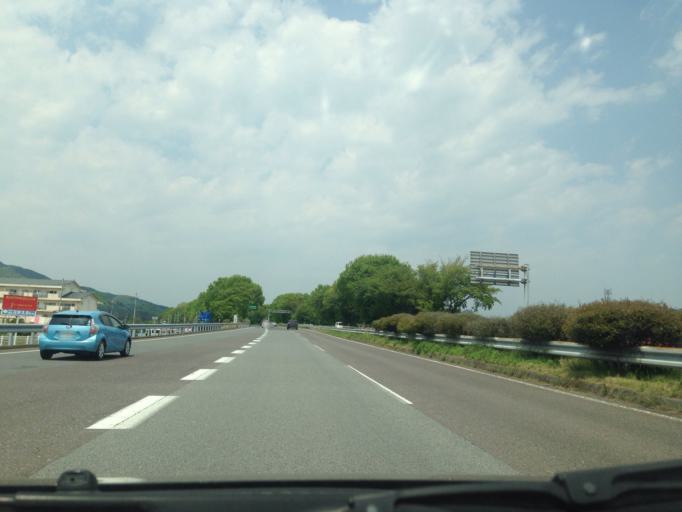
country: JP
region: Tochigi
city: Utsunomiya-shi
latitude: 36.6379
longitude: 139.8451
